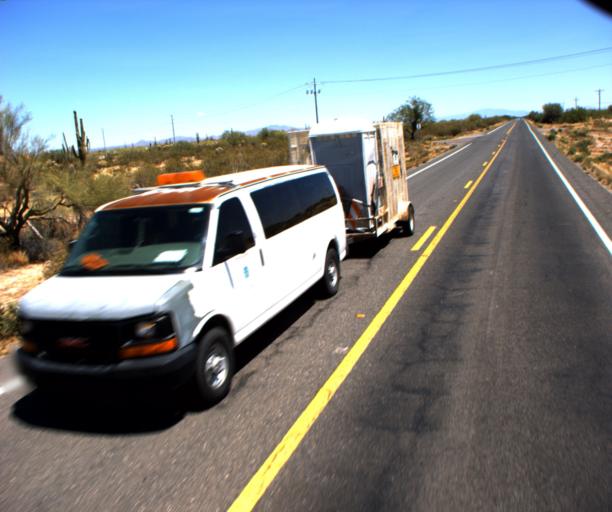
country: US
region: Arizona
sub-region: Pinal County
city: Florence
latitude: 32.9445
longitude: -111.3202
